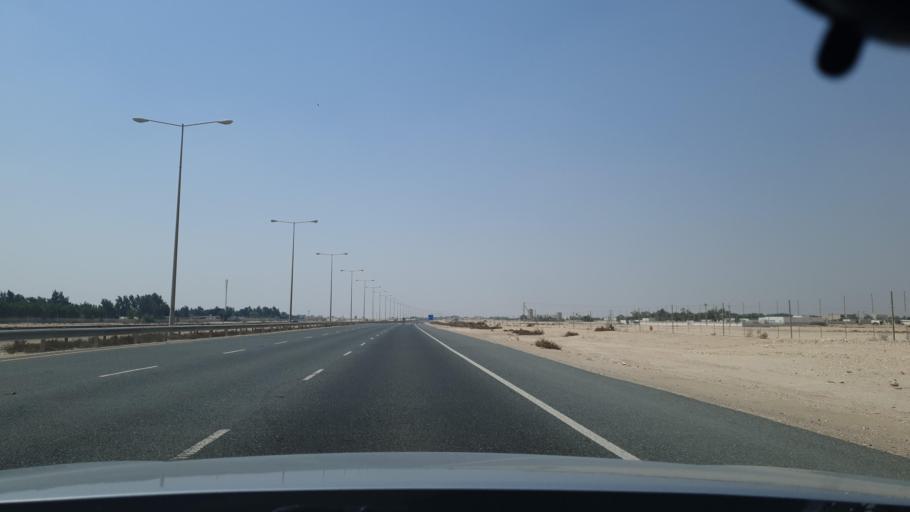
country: QA
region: Al Khawr
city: Al Khawr
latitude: 25.7556
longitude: 51.4546
